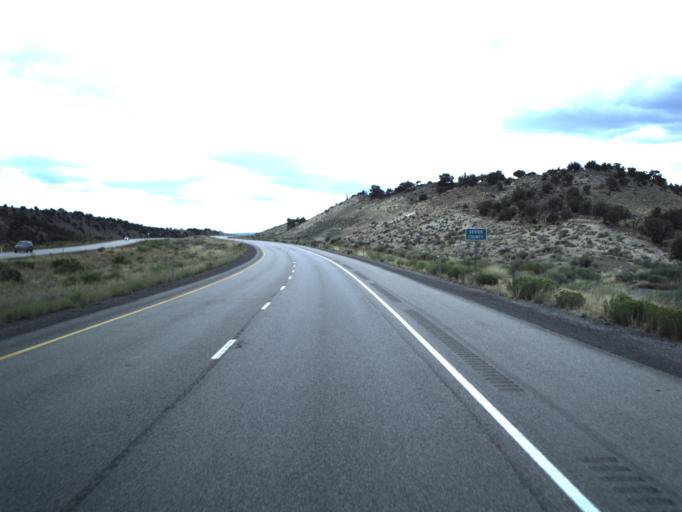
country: US
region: Utah
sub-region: Emery County
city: Ferron
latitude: 38.7891
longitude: -111.2988
